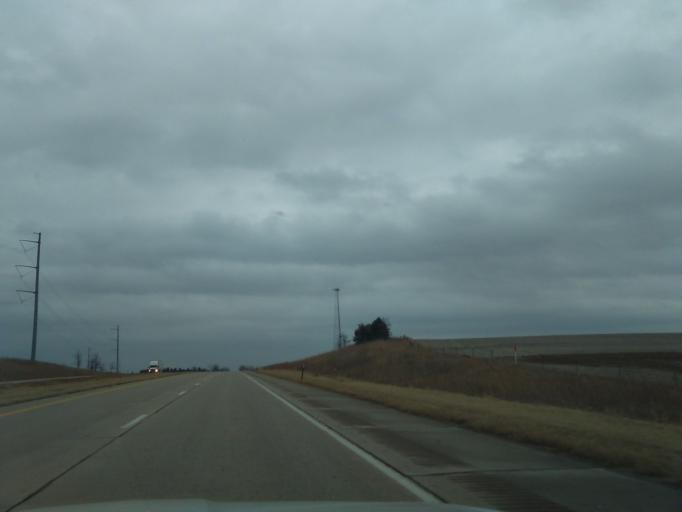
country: US
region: Nebraska
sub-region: Otoe County
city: Syracuse
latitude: 40.6683
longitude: -96.1185
